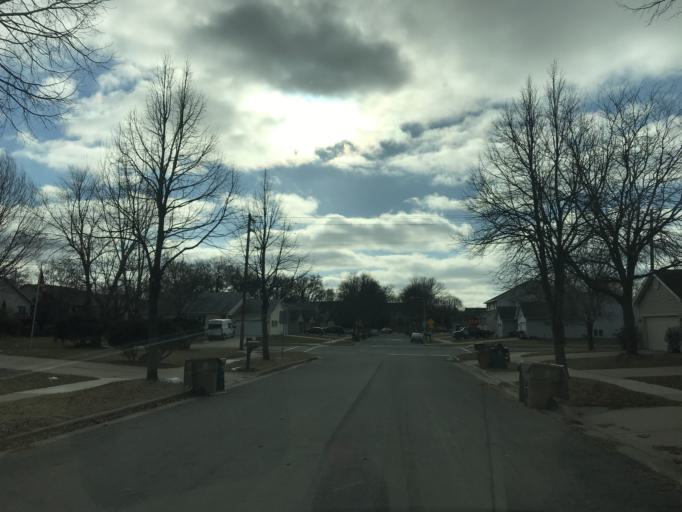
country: US
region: Wisconsin
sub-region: Dane County
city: Monona
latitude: 43.1145
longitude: -89.2973
